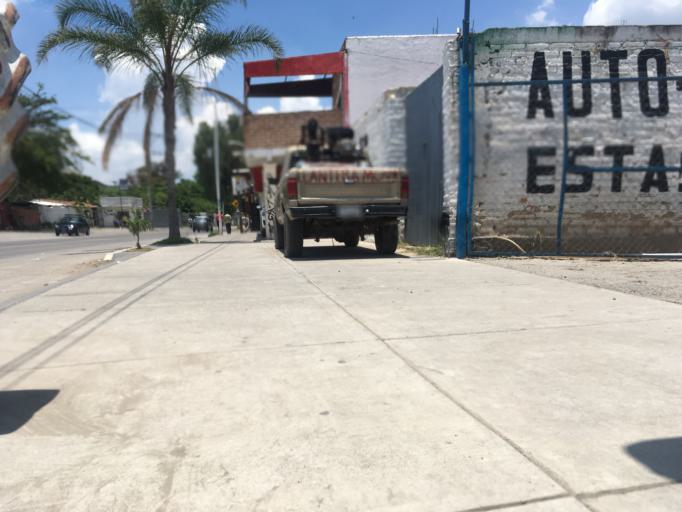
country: MX
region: Jalisco
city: Santa Cruz del Valle
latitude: 20.5292
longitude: -103.4240
